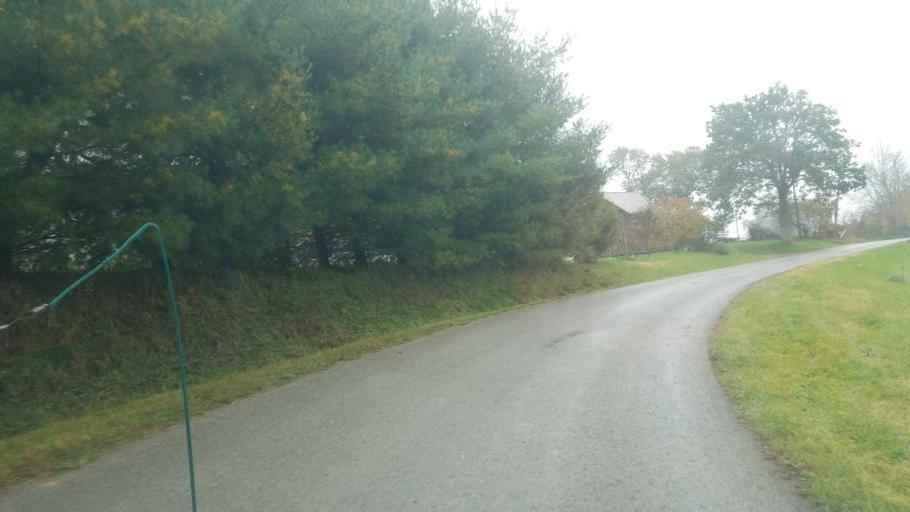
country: US
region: Ohio
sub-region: Morgan County
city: McConnelsville
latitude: 39.5117
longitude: -81.8282
